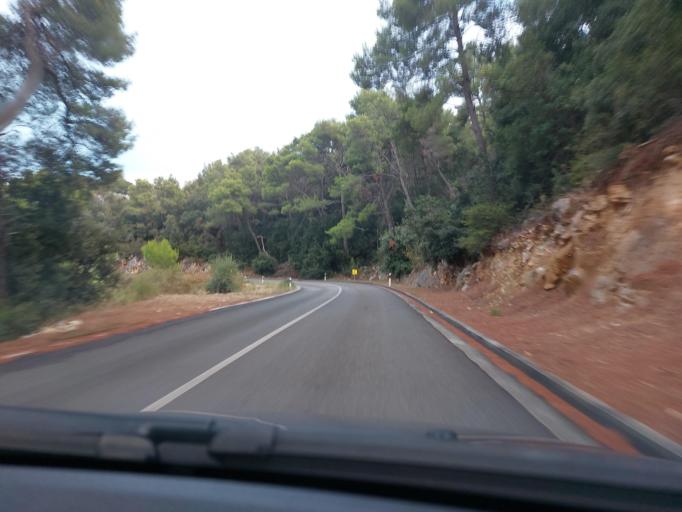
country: HR
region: Dubrovacko-Neretvanska
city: Smokvica
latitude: 42.7675
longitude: 16.8816
